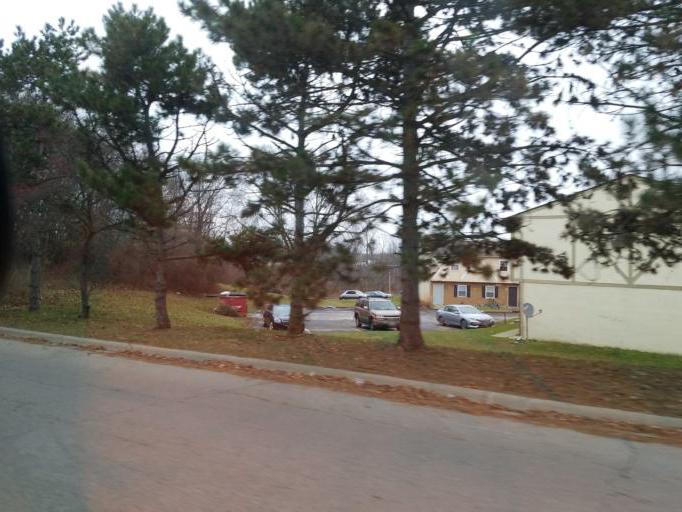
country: US
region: Ohio
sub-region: Franklin County
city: Minerva Park
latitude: 40.1012
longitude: -82.9467
